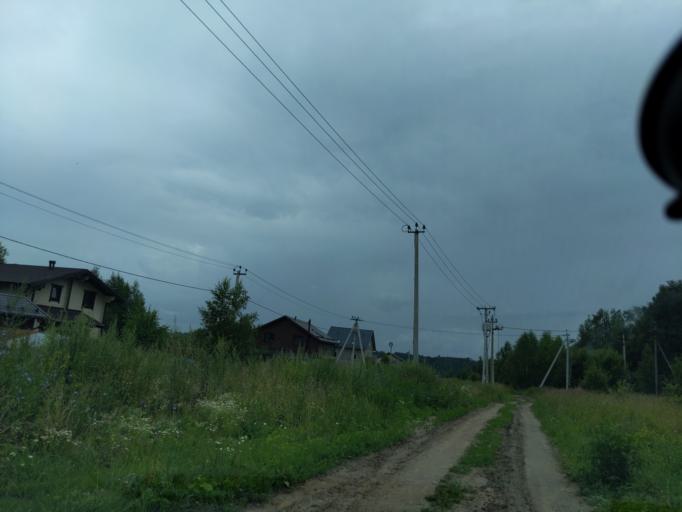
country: RU
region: Moskovskaya
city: Lugovaya
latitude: 56.0592
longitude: 37.5003
